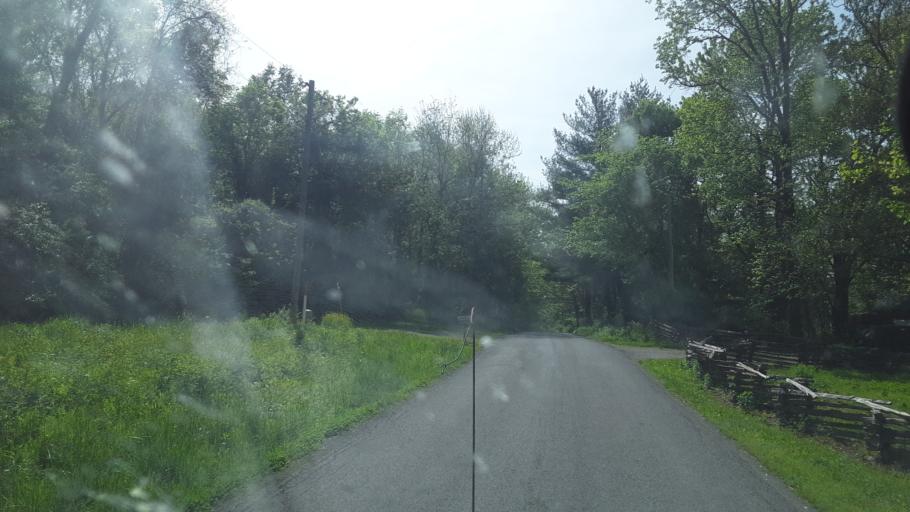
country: US
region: Illinois
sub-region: Jackson County
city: Carbondale
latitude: 37.6807
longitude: -89.2838
